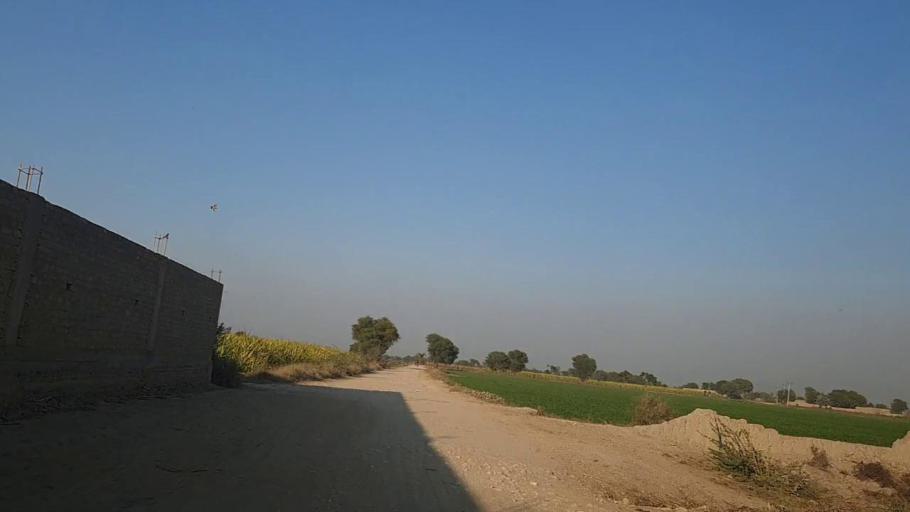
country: PK
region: Sindh
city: Sakrand
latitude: 26.2963
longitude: 68.1228
